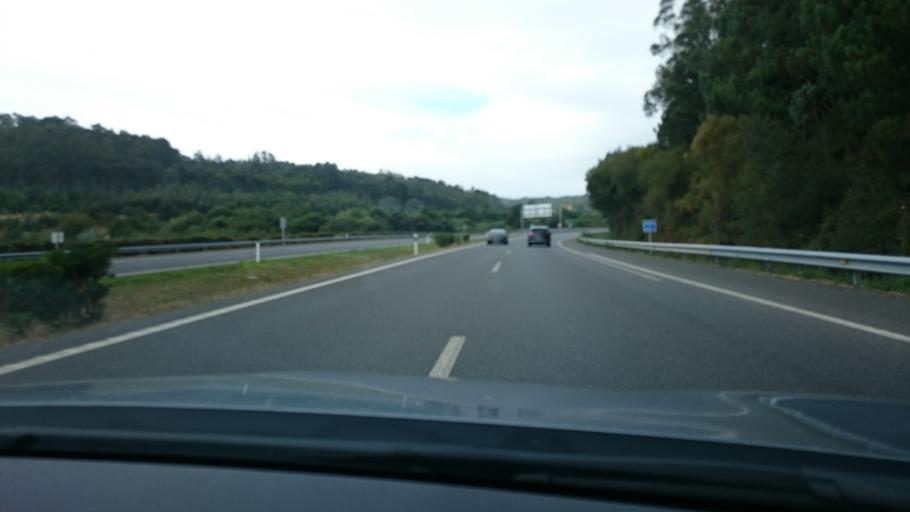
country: ES
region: Galicia
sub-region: Provincia da Coruna
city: Culleredo
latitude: 43.2762
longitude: -8.4124
